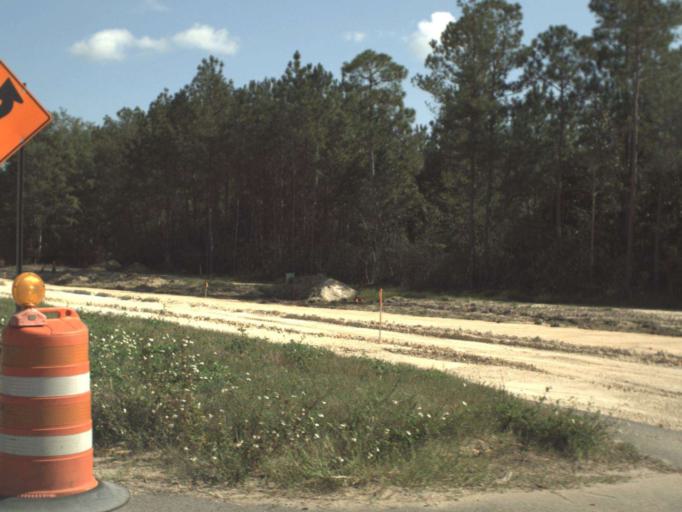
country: US
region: Florida
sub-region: Walton County
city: Freeport
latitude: 30.4874
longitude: -86.1228
